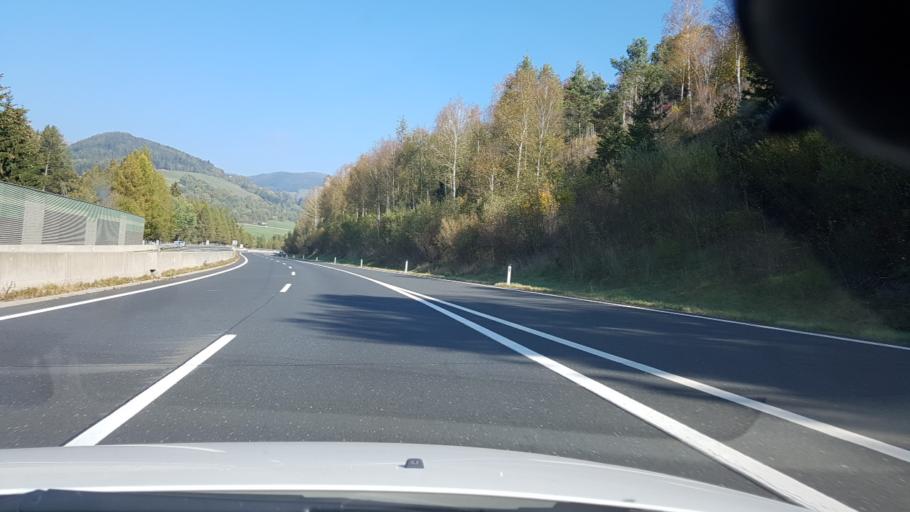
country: AT
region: Carinthia
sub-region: Politischer Bezirk Spittal an der Drau
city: Gmuend
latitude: 46.9021
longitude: 13.5419
